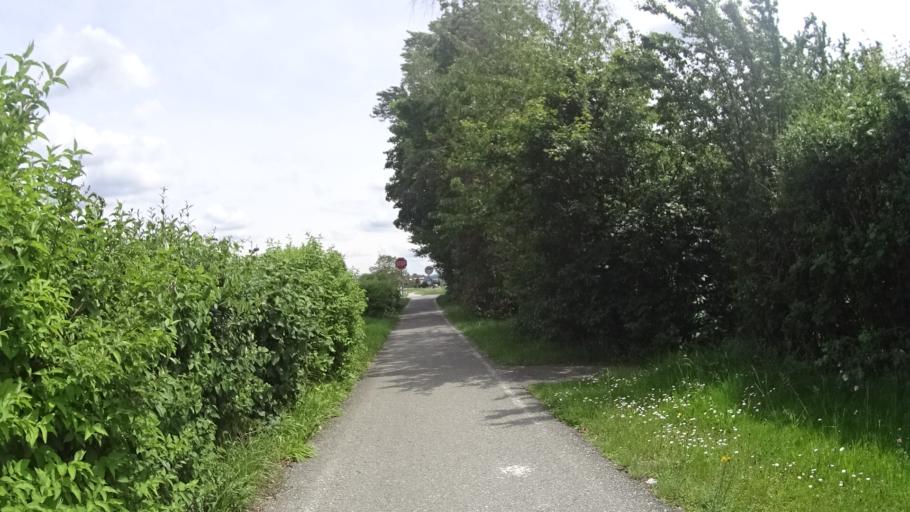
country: DE
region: Baden-Wuerttemberg
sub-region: Freiburg Region
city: Grenzach-Wyhlen
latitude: 47.5463
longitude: 7.6773
